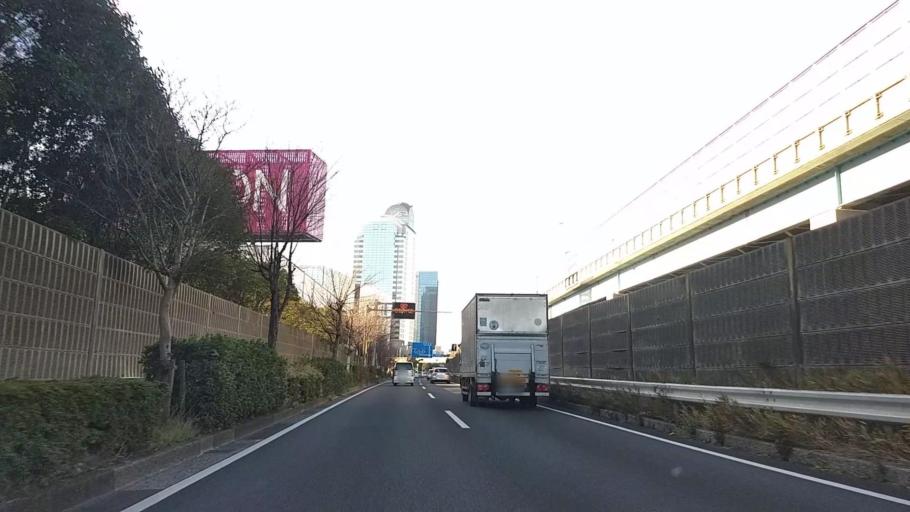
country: JP
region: Chiba
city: Funabashi
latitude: 35.6518
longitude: 140.0475
